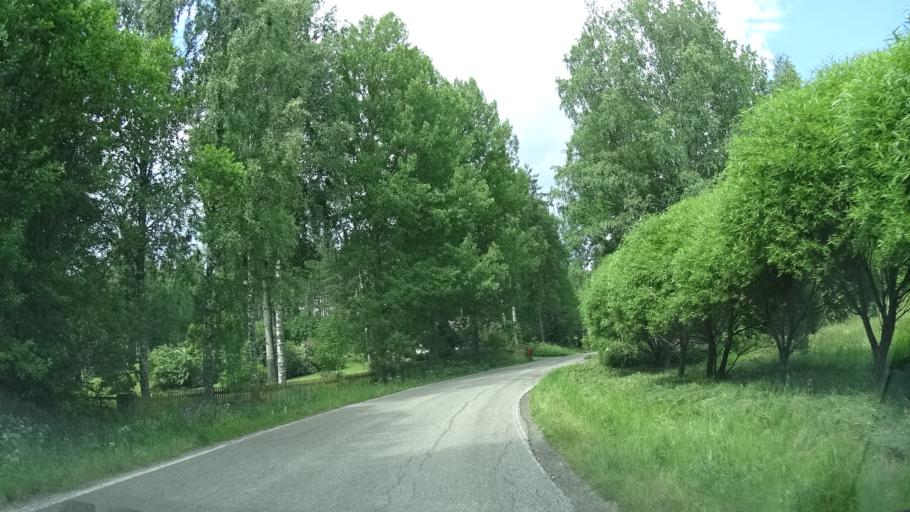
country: FI
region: Uusimaa
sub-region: Helsinki
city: Espoo
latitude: 60.4079
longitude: 24.5912
